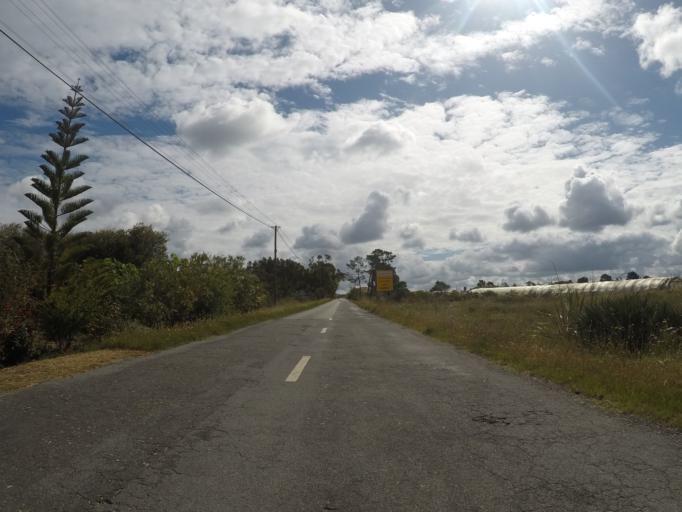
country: PT
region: Beja
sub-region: Odemira
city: Sao Teotonio
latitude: 37.4803
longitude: -8.7729
